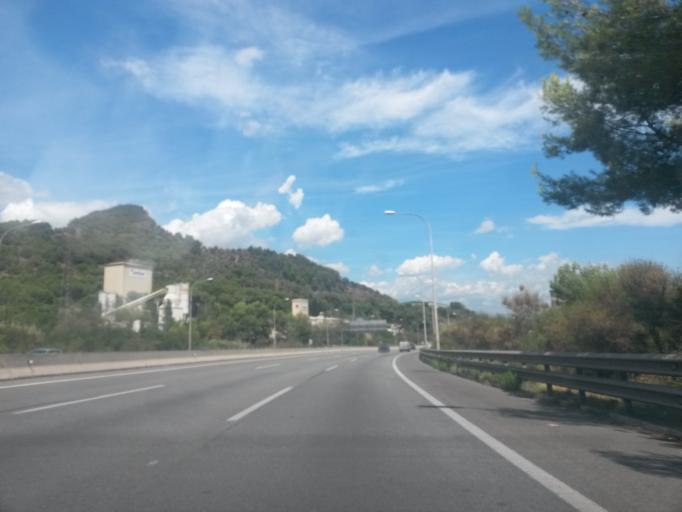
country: ES
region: Catalonia
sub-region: Provincia de Barcelona
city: Montcada i Reixac
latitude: 41.4692
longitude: 2.1776
